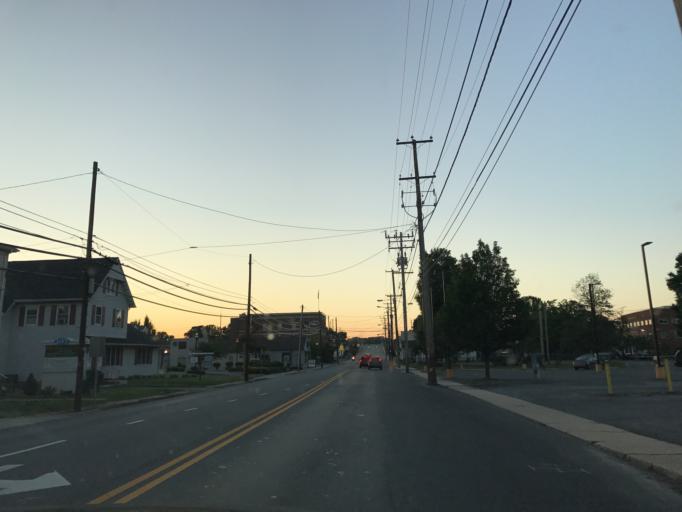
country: US
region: Maryland
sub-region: Cecil County
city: Elkton
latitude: 39.6070
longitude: -75.8333
